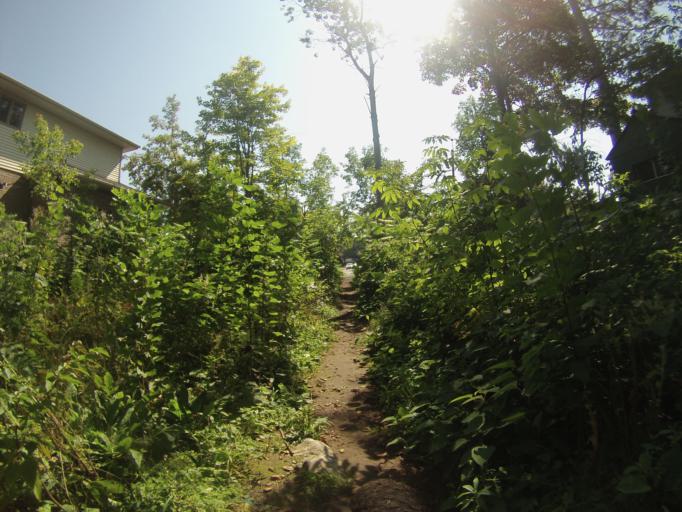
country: CA
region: Ontario
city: Ottawa
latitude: 45.3521
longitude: -75.6192
